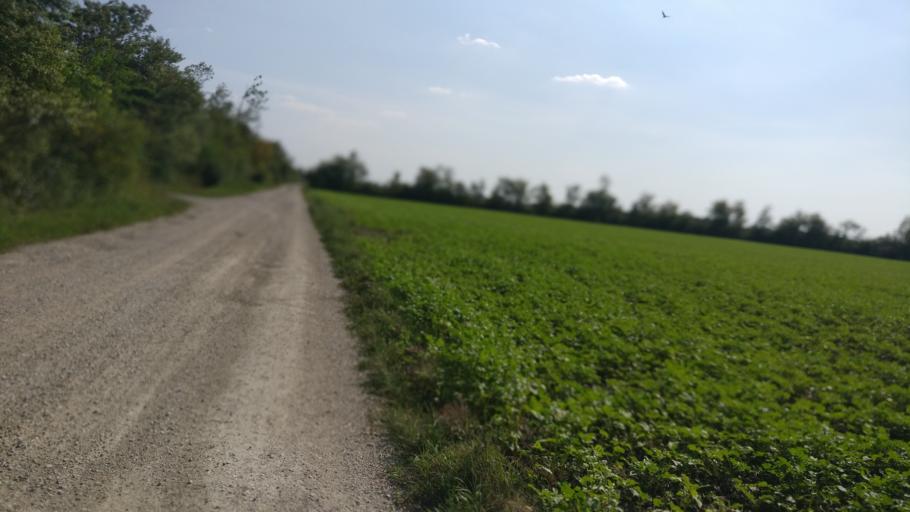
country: AT
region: Lower Austria
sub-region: Politischer Bezirk Modling
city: Munchendorf
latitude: 47.9990
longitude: 16.3957
